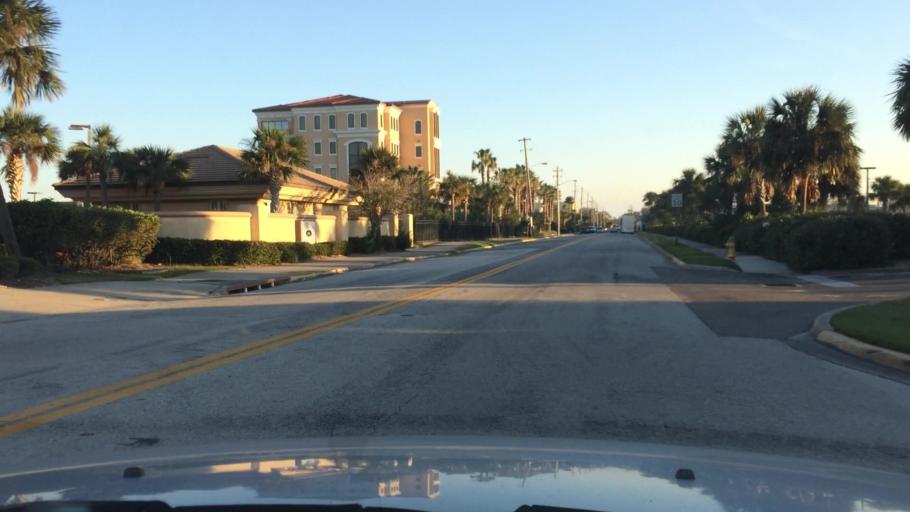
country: US
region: Florida
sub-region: Volusia County
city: Daytona Beach
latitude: 29.2293
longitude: -81.0248
